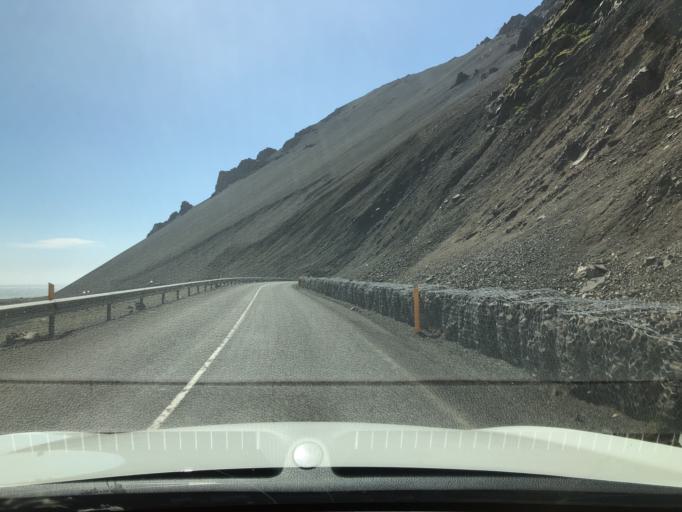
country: IS
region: East
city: Reydarfjoerdur
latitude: 64.4518
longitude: -14.5119
